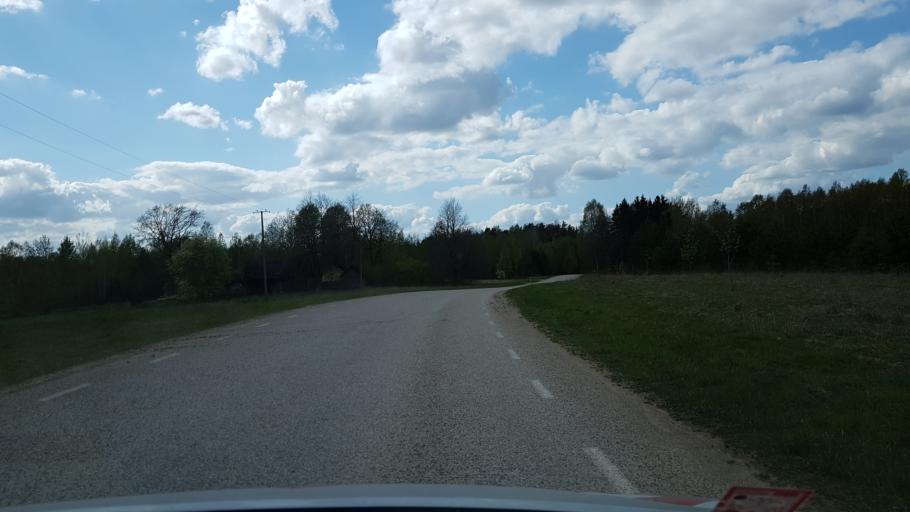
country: EE
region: Tartu
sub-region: UElenurme vald
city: Ulenurme
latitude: 58.3450
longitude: 26.8183
